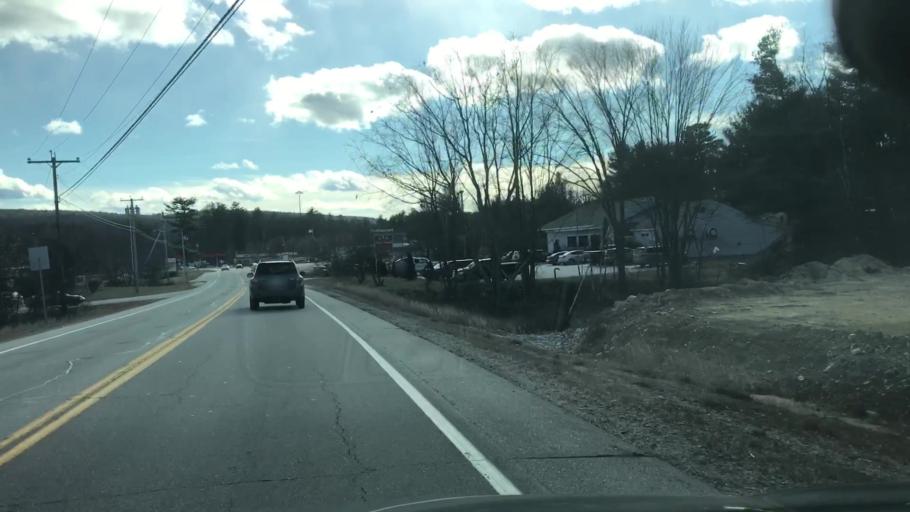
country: US
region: New Hampshire
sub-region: Merrimack County
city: Epsom
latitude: 43.2310
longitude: -71.3611
